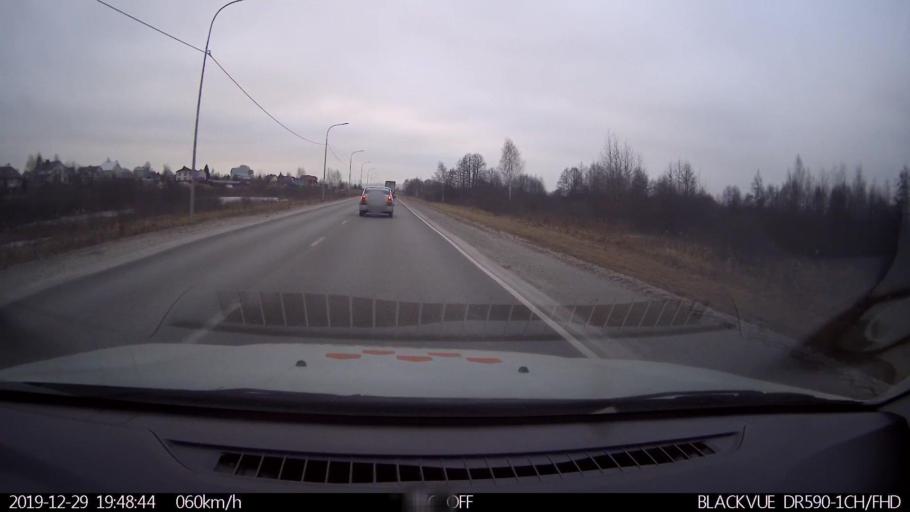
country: RU
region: Nizjnij Novgorod
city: Neklyudovo
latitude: 56.3835
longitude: 44.0098
